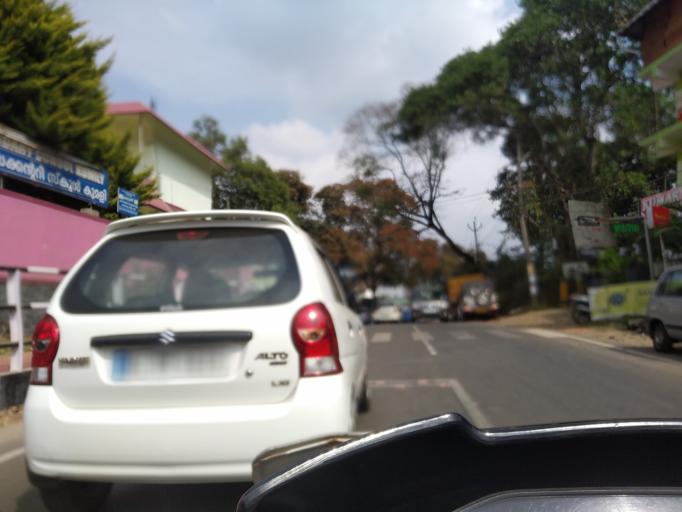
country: IN
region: Tamil Nadu
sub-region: Theni
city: Gudalur
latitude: 9.6091
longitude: 77.1666
